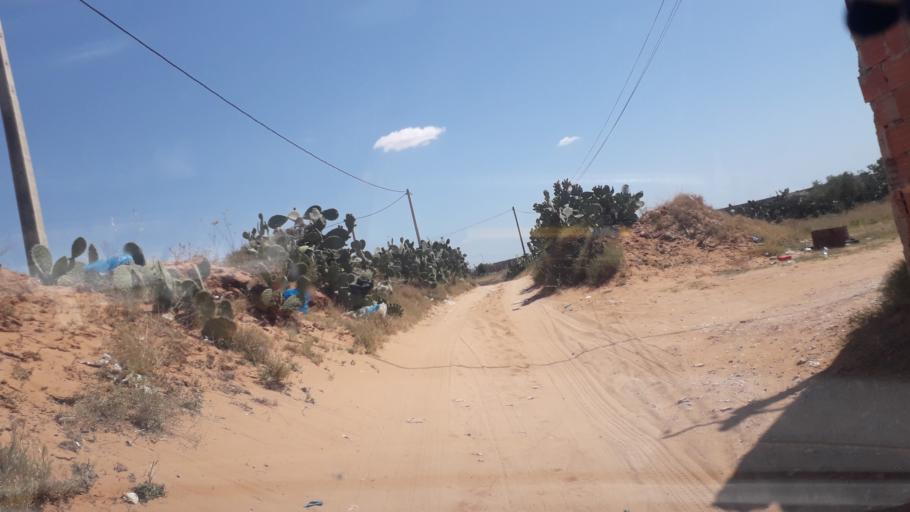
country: TN
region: Safaqis
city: Al Qarmadah
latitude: 34.8328
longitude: 10.7713
